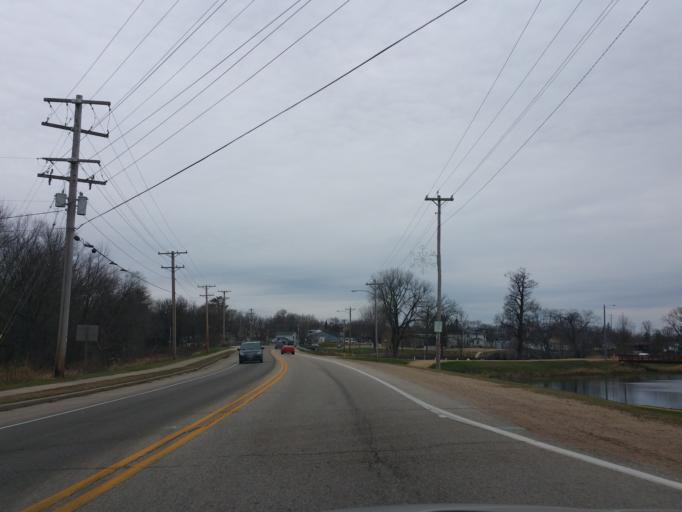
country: US
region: Wisconsin
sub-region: Juneau County
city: New Lisbon
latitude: 43.8808
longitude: -90.1593
